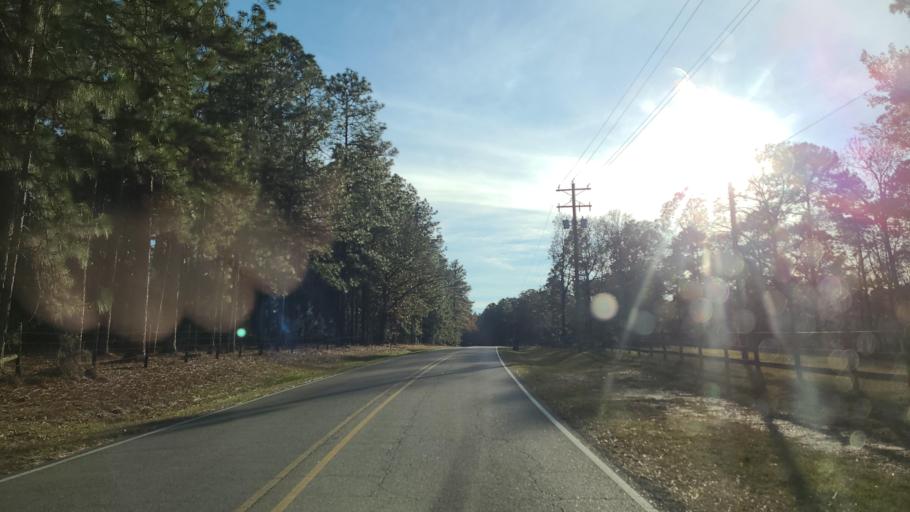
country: US
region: Mississippi
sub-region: Lamar County
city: Purvis
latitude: 31.1786
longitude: -89.2925
